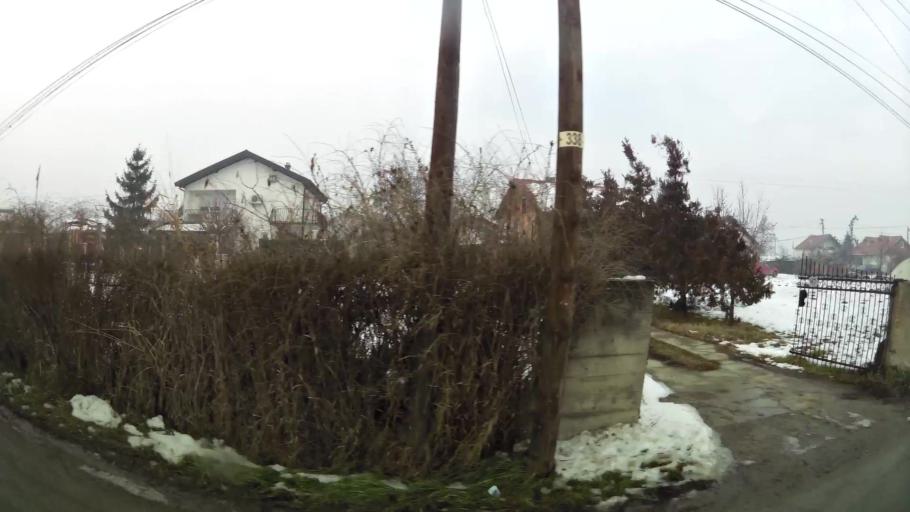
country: MK
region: Ilinden
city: Jurumleri
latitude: 41.9700
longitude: 21.5564
